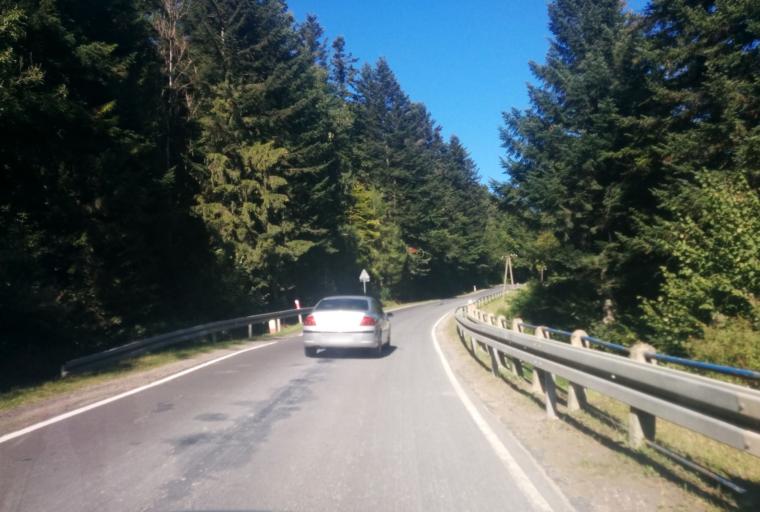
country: PL
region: Subcarpathian Voivodeship
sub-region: Powiat bieszczadzki
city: Lutowiska
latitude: 49.2770
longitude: 22.6850
